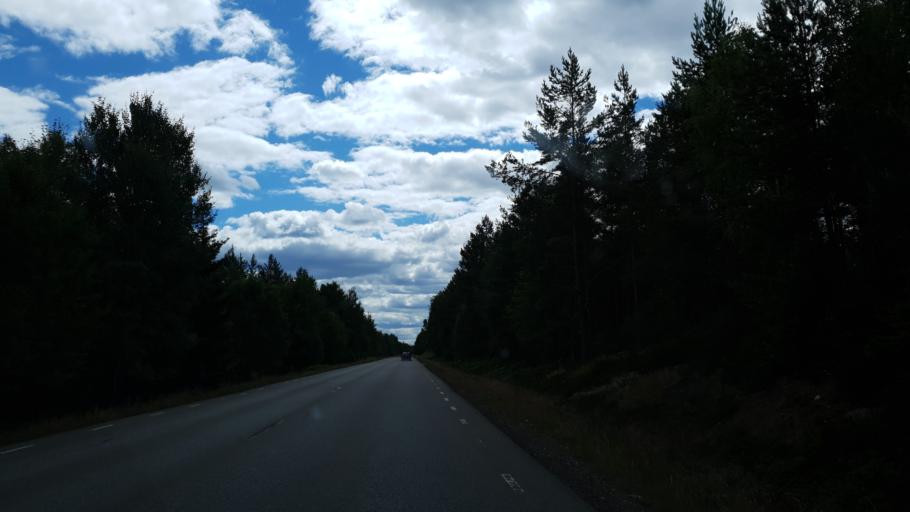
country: SE
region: Kronoberg
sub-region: Uppvidinge Kommun
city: Lenhovda
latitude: 56.9455
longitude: 15.5850
